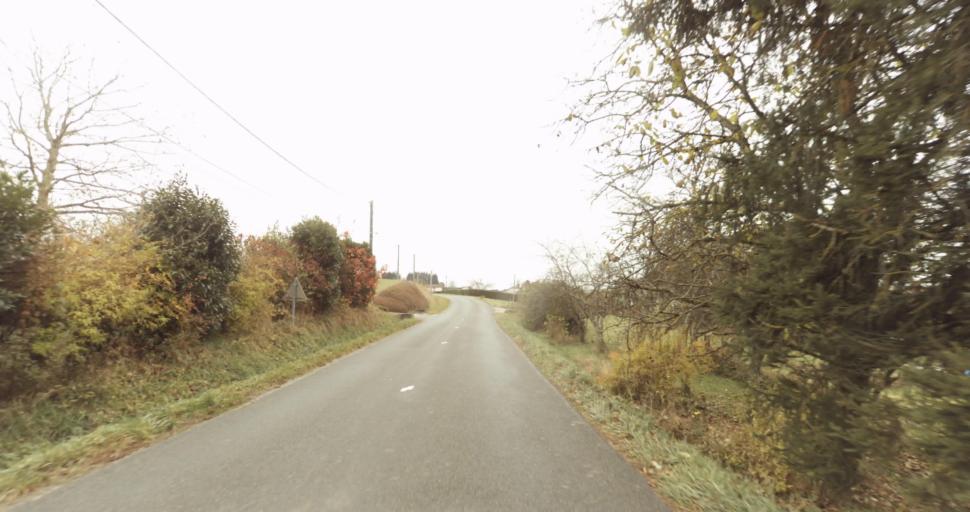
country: FR
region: Rhone-Alpes
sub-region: Departement de la Haute-Savoie
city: Groisy
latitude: 46.0421
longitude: 6.1857
